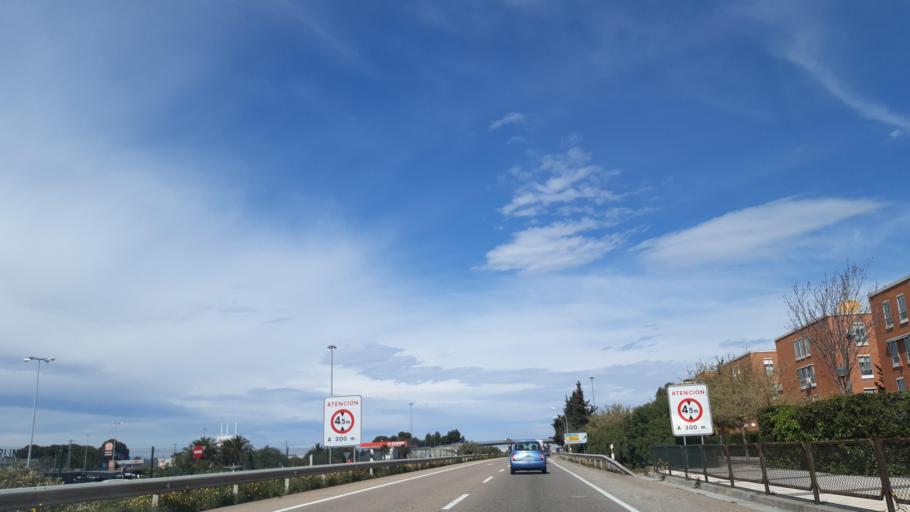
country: ES
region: Aragon
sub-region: Provincia de Zaragoza
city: Utebo
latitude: 41.7027
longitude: -1.0016
